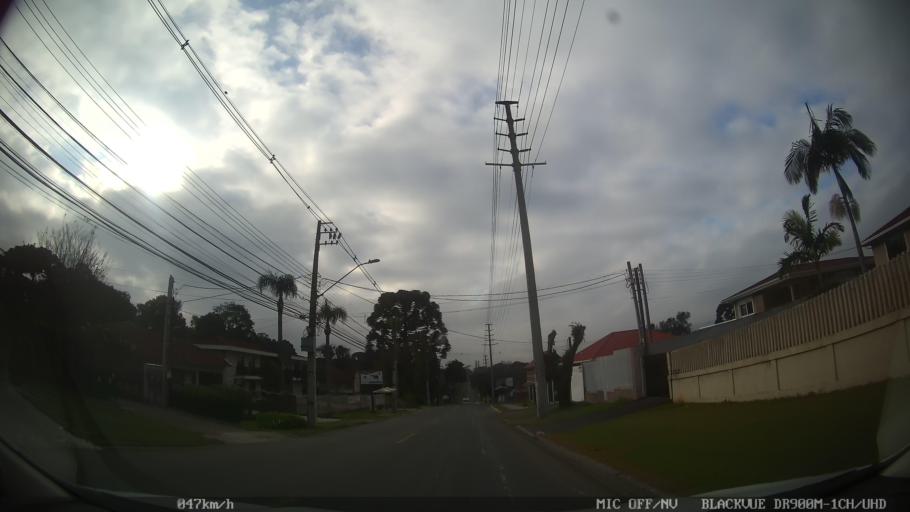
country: BR
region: Parana
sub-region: Curitiba
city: Curitiba
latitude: -25.3927
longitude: -49.3330
